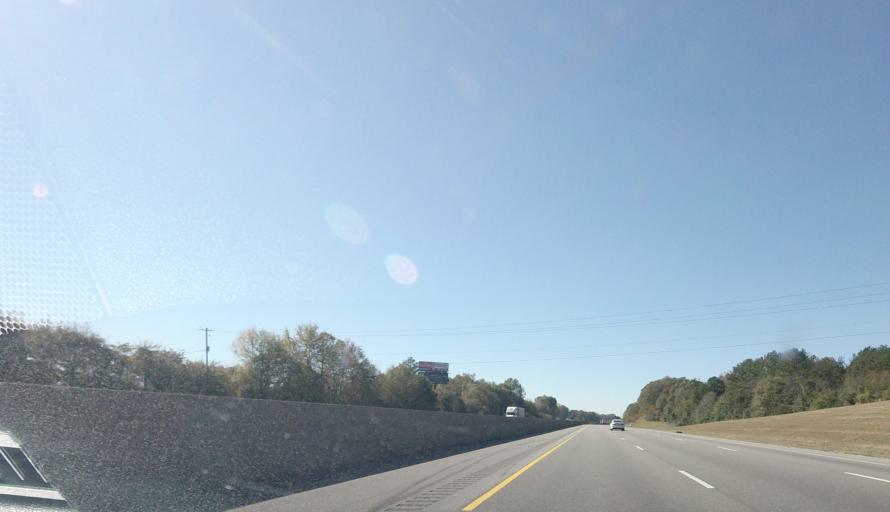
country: US
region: Alabama
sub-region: Calhoun County
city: Oxford
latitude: 33.5988
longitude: -85.8498
